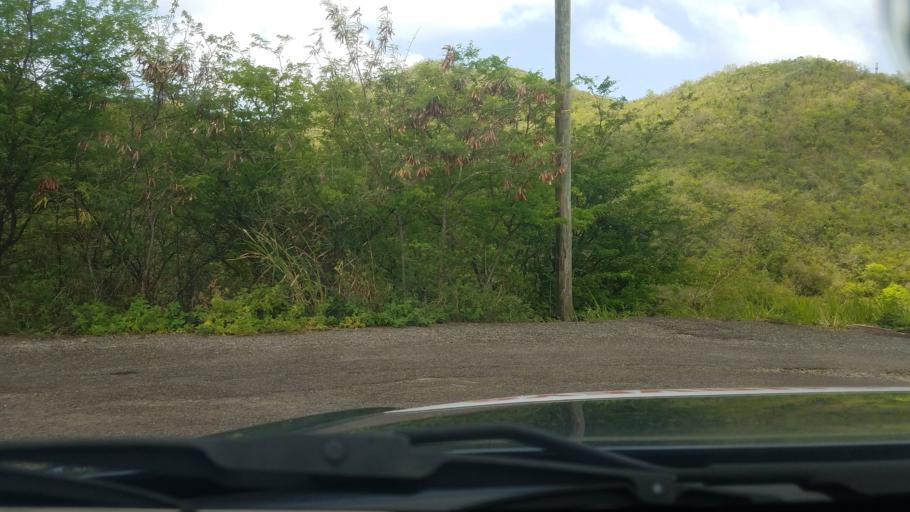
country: LC
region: Gros-Islet
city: Gros Islet
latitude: 14.0585
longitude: -60.9309
